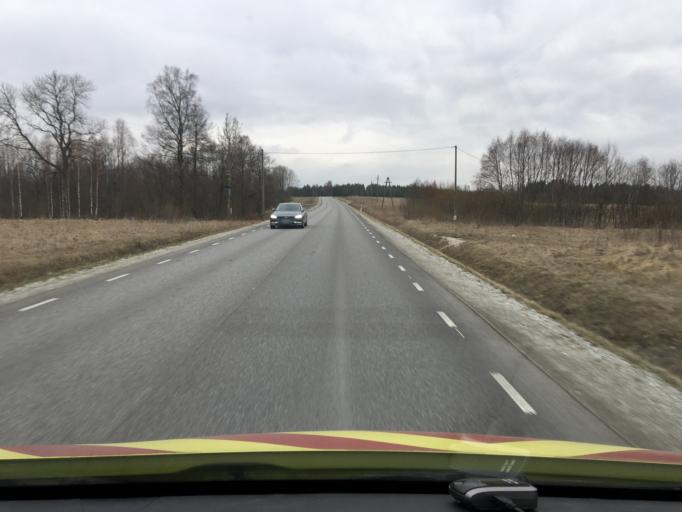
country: EE
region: Raplamaa
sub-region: Rapla vald
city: Rapla
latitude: 59.0014
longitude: 24.8426
